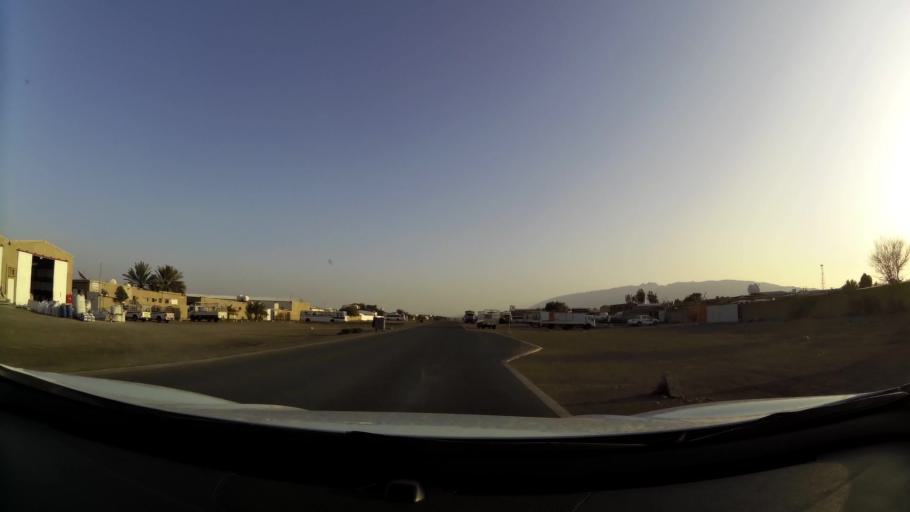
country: AE
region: Abu Dhabi
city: Al Ain
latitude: 24.1567
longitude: 55.8187
